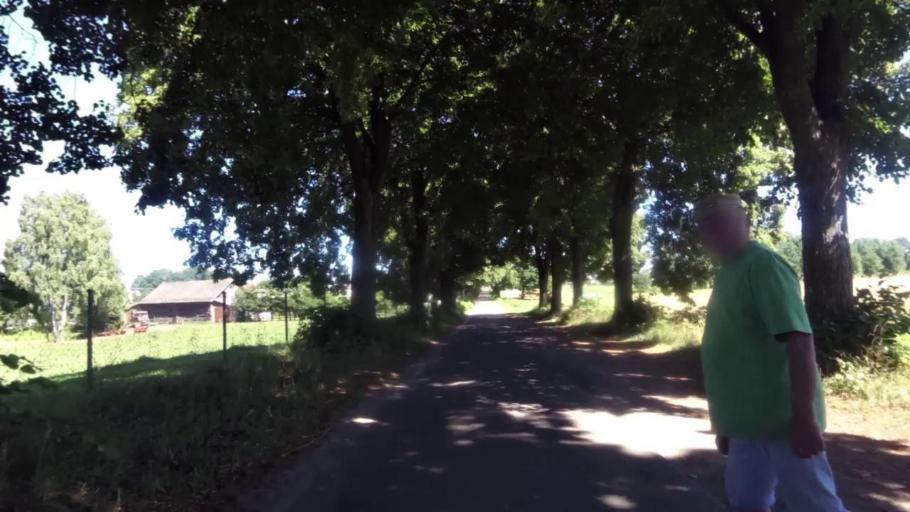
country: PL
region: West Pomeranian Voivodeship
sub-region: Powiat szczecinecki
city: Bialy Bor
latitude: 53.8877
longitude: 16.9320
